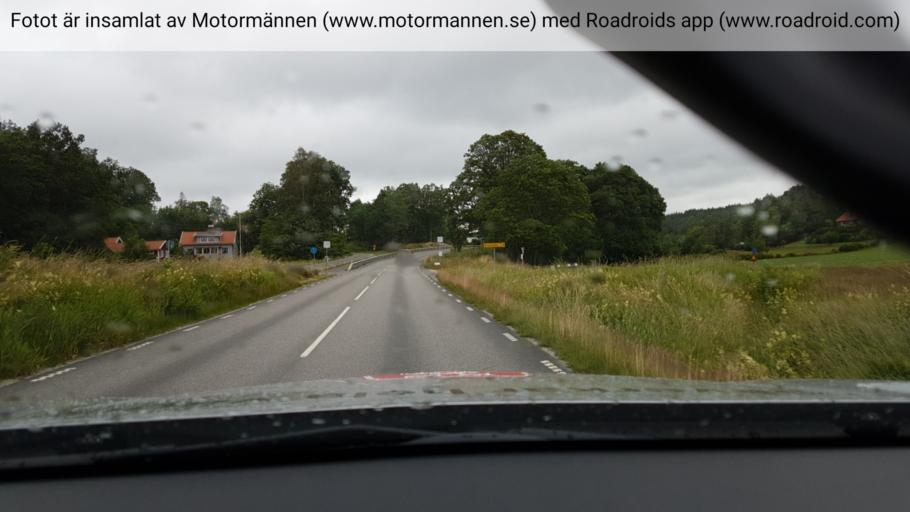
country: SE
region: Vaestra Goetaland
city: Svanesund
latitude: 58.1213
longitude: 11.8553
